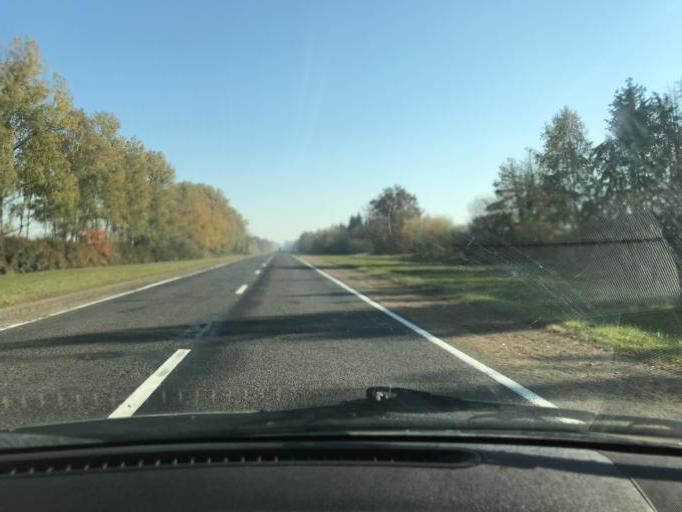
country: BY
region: Minsk
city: Klyetsk
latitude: 52.9652
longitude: 26.5202
